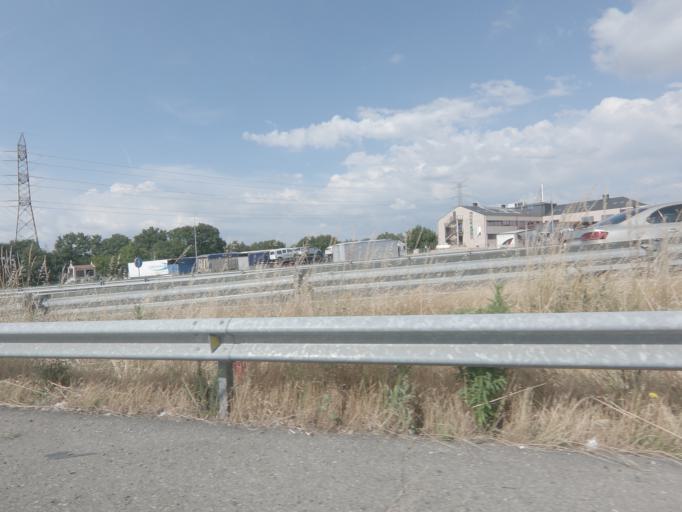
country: ES
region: Galicia
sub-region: Provincia de Ourense
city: Taboadela
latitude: 42.2506
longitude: -7.8659
